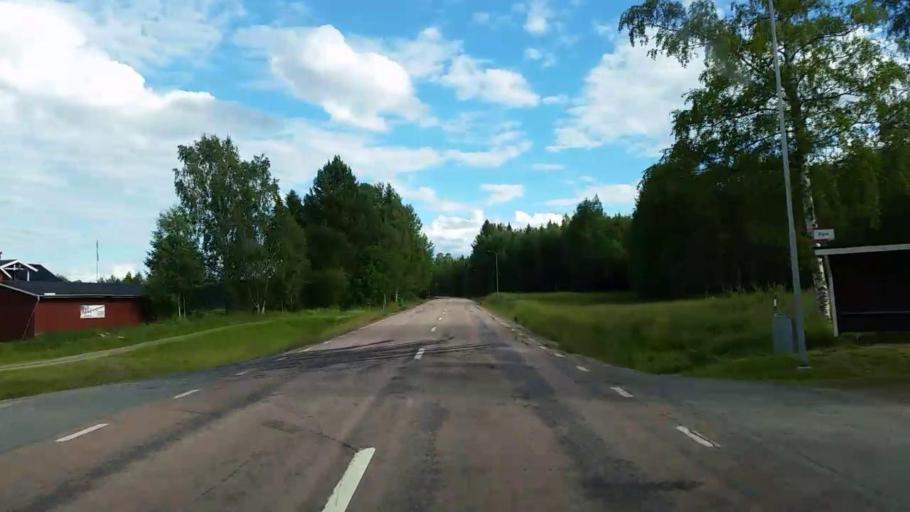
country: SE
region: Gaevleborg
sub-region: Ljusdals Kommun
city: Farila
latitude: 61.9013
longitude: 15.8981
